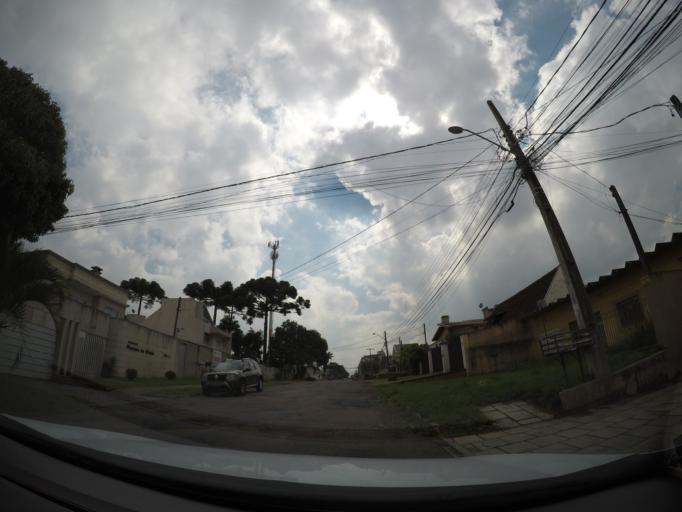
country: BR
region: Parana
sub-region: Sao Jose Dos Pinhais
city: Sao Jose dos Pinhais
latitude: -25.4888
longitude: -49.2534
